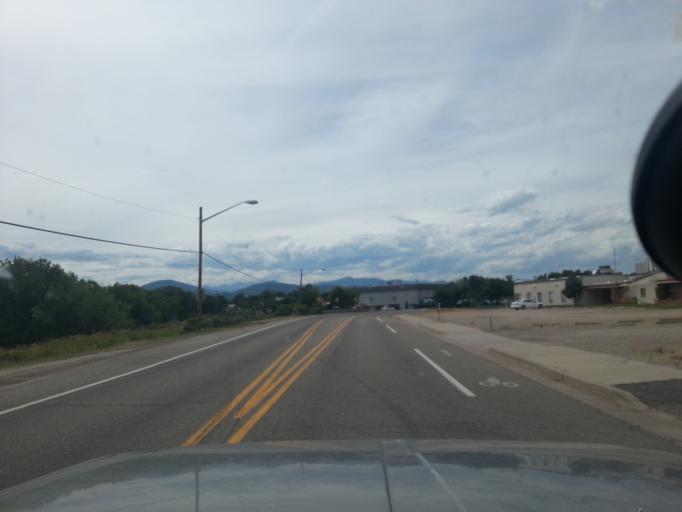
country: US
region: Colorado
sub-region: Larimer County
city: Loveland
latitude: 40.4020
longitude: -105.1080
